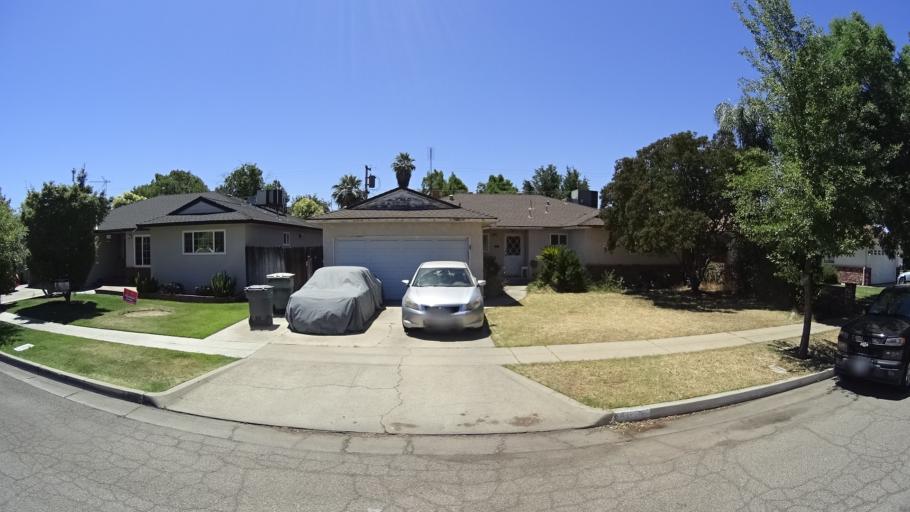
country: US
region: California
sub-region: Fresno County
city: Fresno
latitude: 36.8032
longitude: -119.7660
